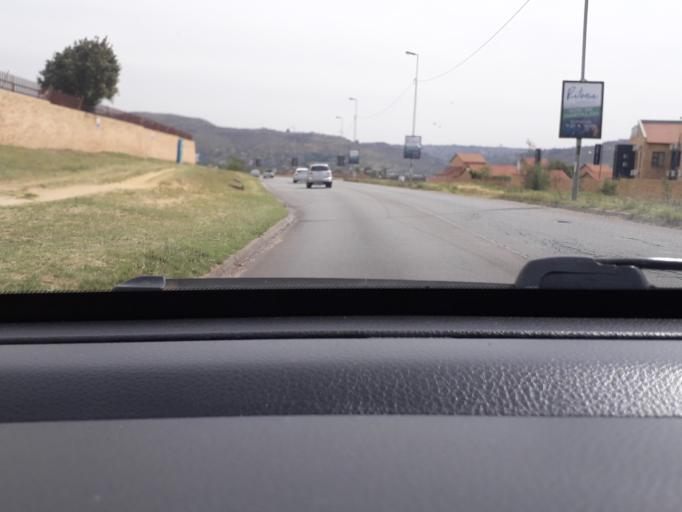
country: ZA
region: Gauteng
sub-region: City of Johannesburg Metropolitan Municipality
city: Roodepoort
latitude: -26.1015
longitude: 27.9016
